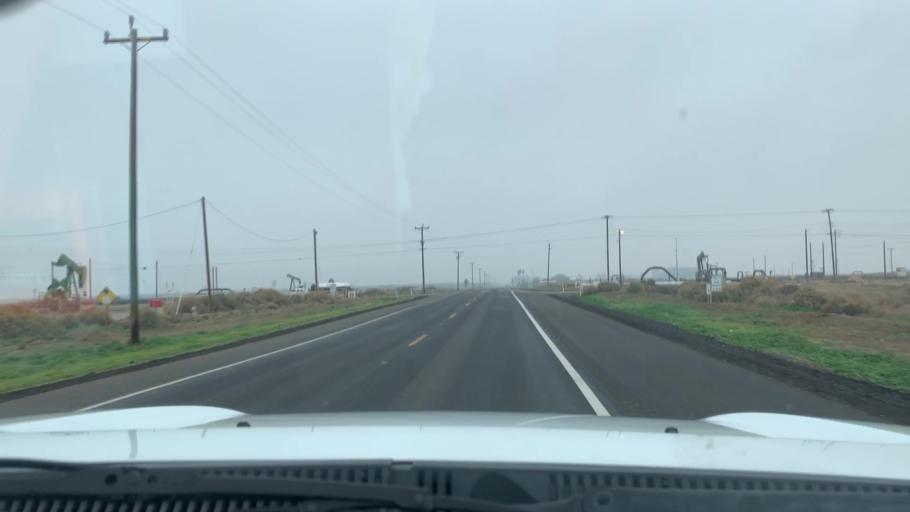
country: US
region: California
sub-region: Kern County
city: Lost Hills
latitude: 35.6159
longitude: -119.7177
